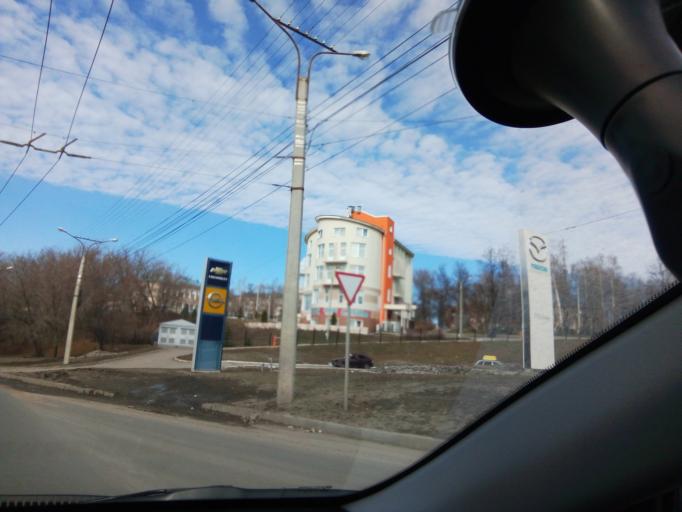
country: RU
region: Chuvashia
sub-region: Cheboksarskiy Rayon
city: Cheboksary
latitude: 56.1166
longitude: 47.2542
